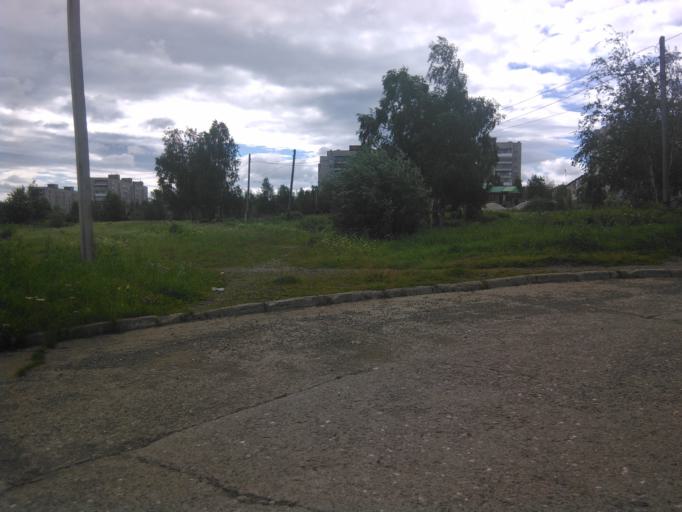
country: RU
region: Sverdlovsk
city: Krasnotur'insk
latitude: 59.7607
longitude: 60.1664
